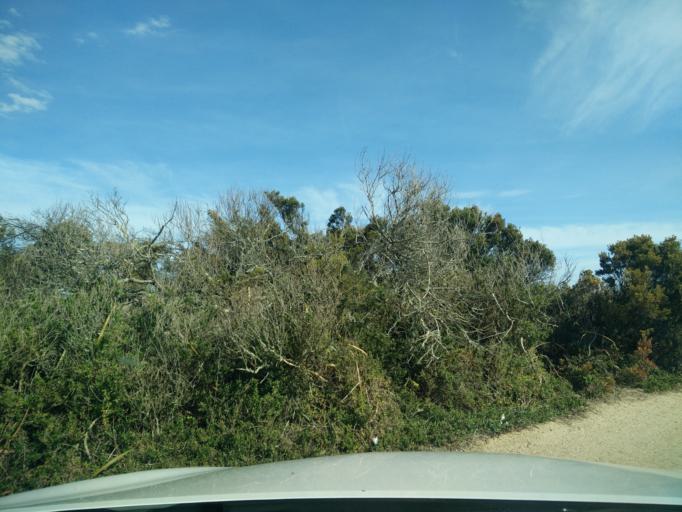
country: AU
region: Tasmania
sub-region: Break O'Day
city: St Helens
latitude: -41.3997
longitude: 148.2877
